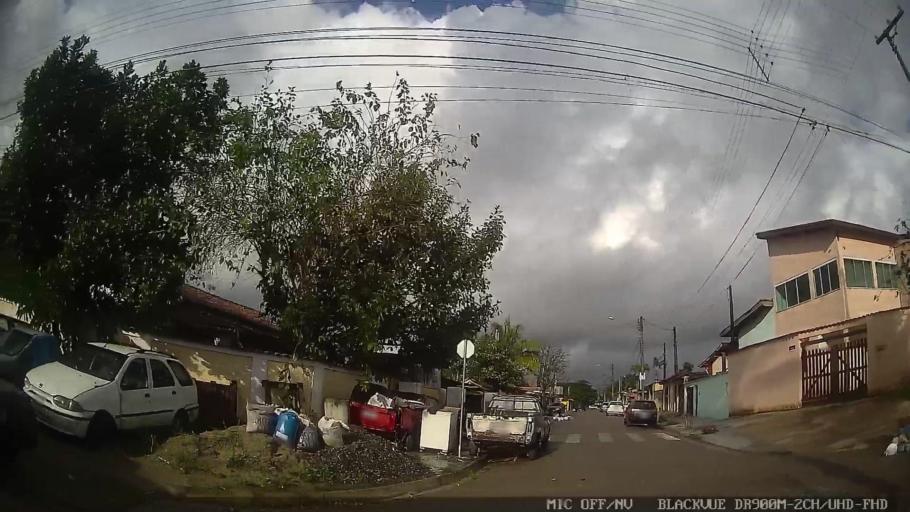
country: BR
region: Sao Paulo
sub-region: Itanhaem
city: Itanhaem
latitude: -24.2111
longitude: -46.8790
